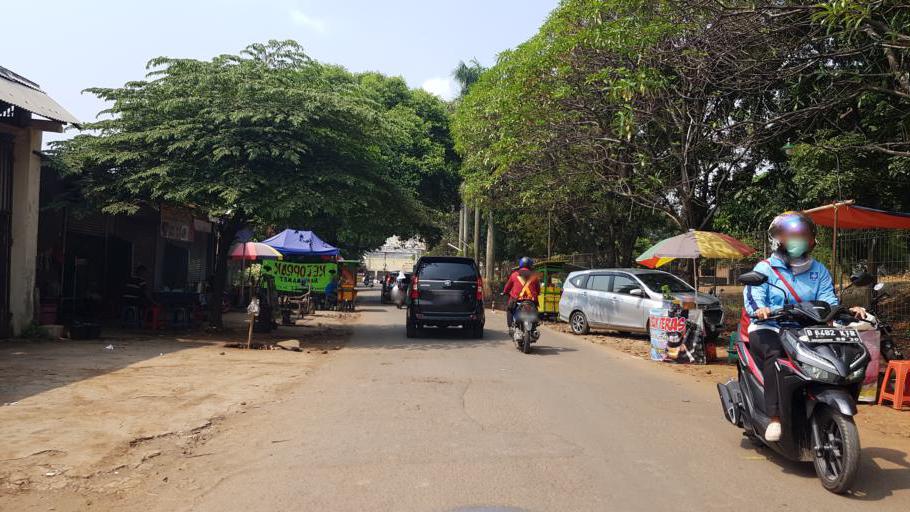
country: ID
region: West Java
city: Bekasi
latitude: -6.2845
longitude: 106.9298
